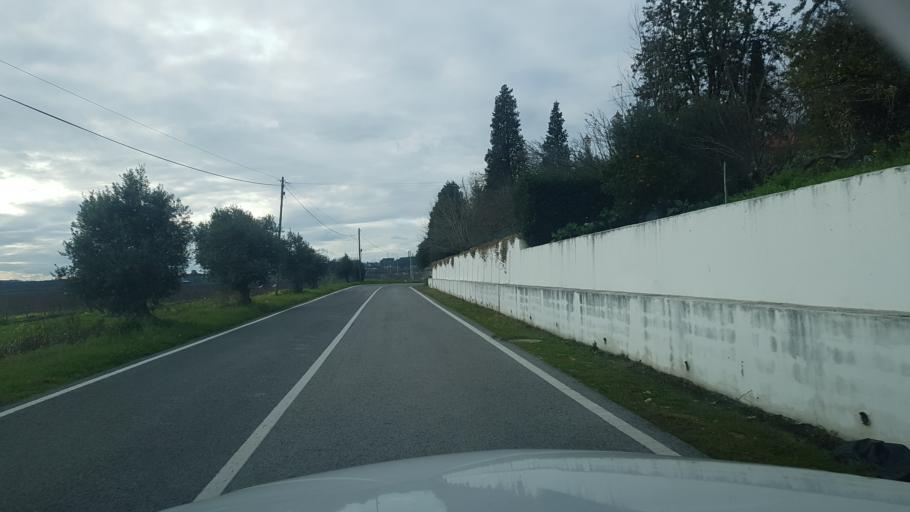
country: PT
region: Santarem
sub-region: Abrantes
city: Tramagal
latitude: 39.4831
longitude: -8.2534
